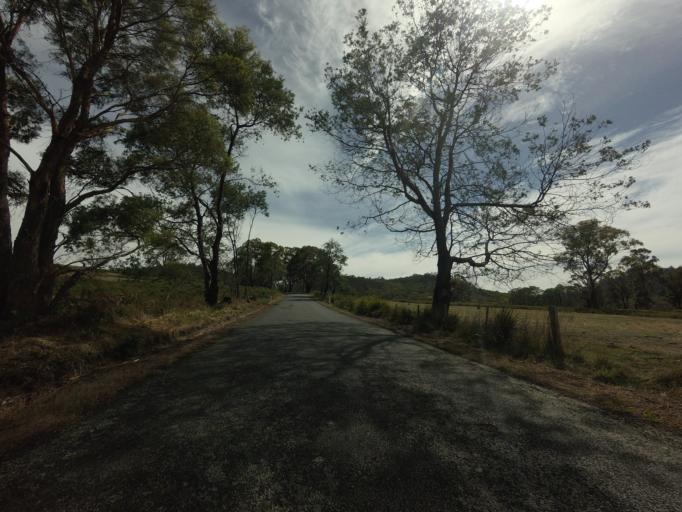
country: AU
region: Tasmania
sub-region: Sorell
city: Sorell
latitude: -42.5739
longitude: 147.6942
